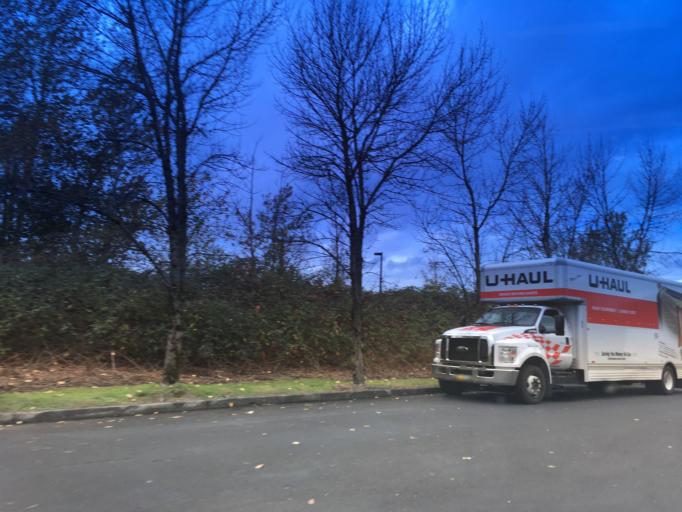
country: US
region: Oregon
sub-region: Multnomah County
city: Fairview
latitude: 45.5277
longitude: -122.4513
